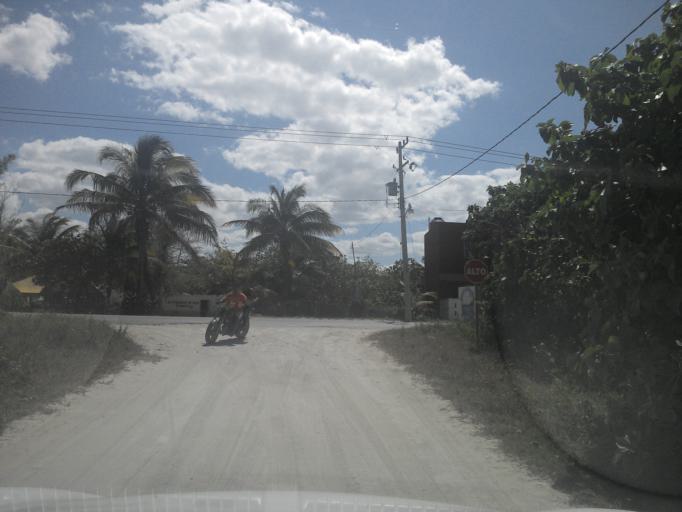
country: MX
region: Yucatan
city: Telchac Puerto
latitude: 21.3412
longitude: -89.2791
